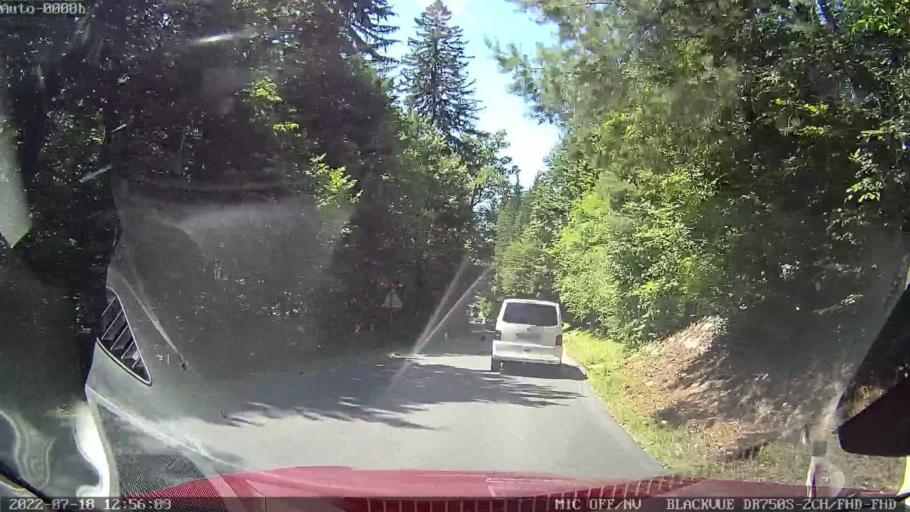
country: SI
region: Dobrova-Horjul-Polhov Gradec
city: Dobrova
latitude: 46.0729
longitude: 14.4349
